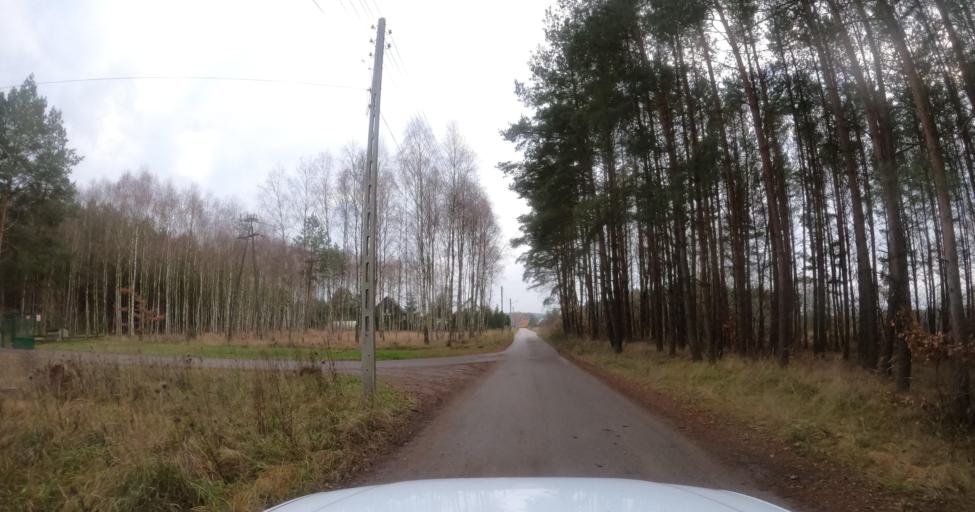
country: PL
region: West Pomeranian Voivodeship
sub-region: Powiat goleniowski
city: Przybiernow
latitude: 53.7618
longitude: 14.7451
